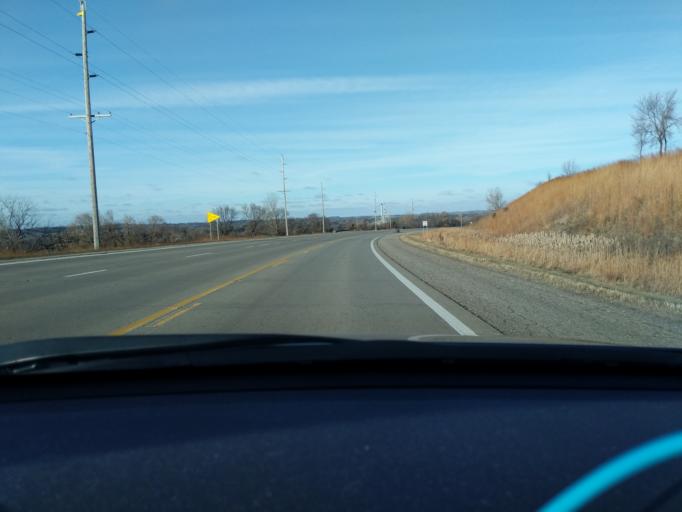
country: US
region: Minnesota
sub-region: Yellow Medicine County
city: Granite Falls
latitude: 44.7967
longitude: -95.5040
